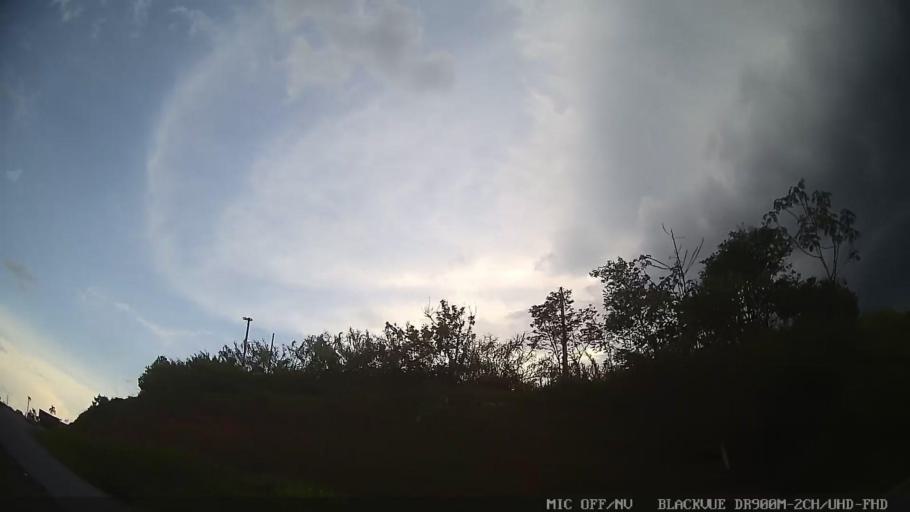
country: BR
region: Sao Paulo
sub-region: Itatiba
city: Itatiba
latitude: -22.9771
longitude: -46.8369
